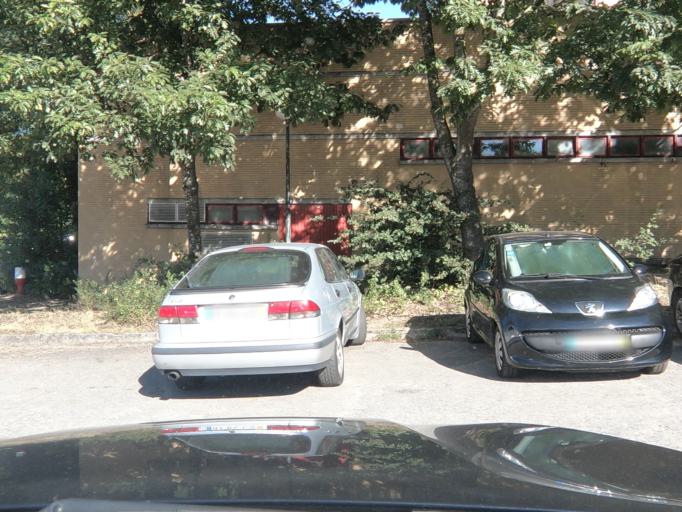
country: PT
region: Vila Real
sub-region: Vila Real
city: Vila Real
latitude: 41.2882
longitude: -7.7421
